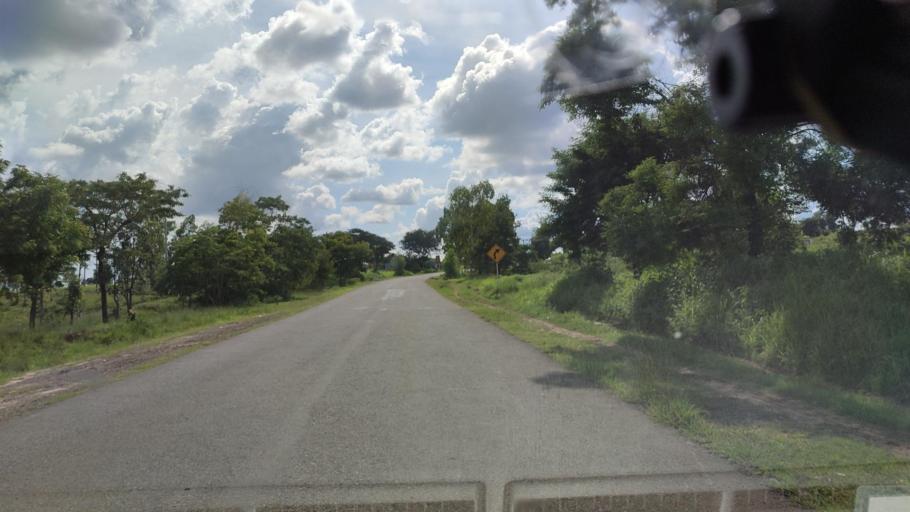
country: MM
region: Mandalay
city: Meiktila
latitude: 20.8032
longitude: 95.5713
